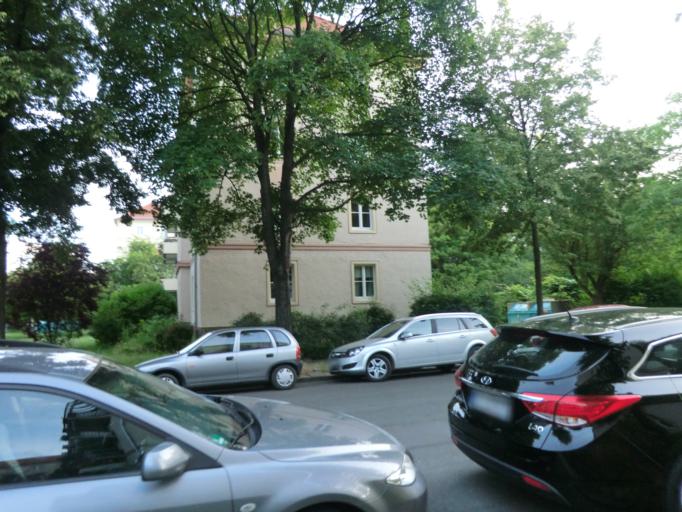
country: DE
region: Saxony
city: Dresden
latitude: 51.0363
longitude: 13.7203
